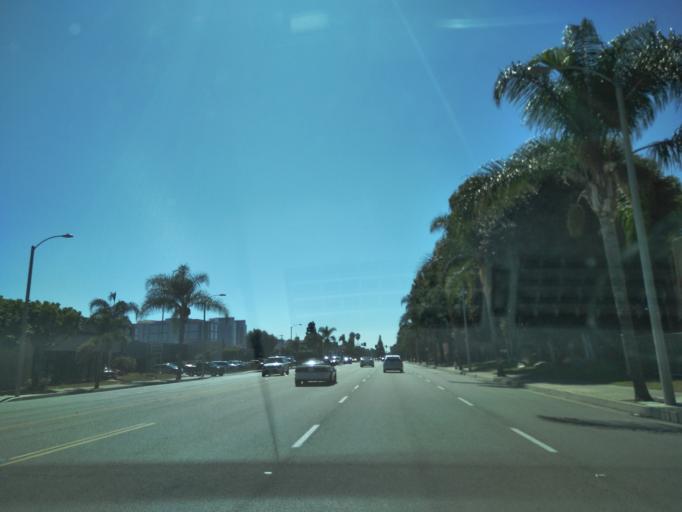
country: US
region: California
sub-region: Orange County
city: Santa Ana
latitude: 33.7072
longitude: -117.8682
